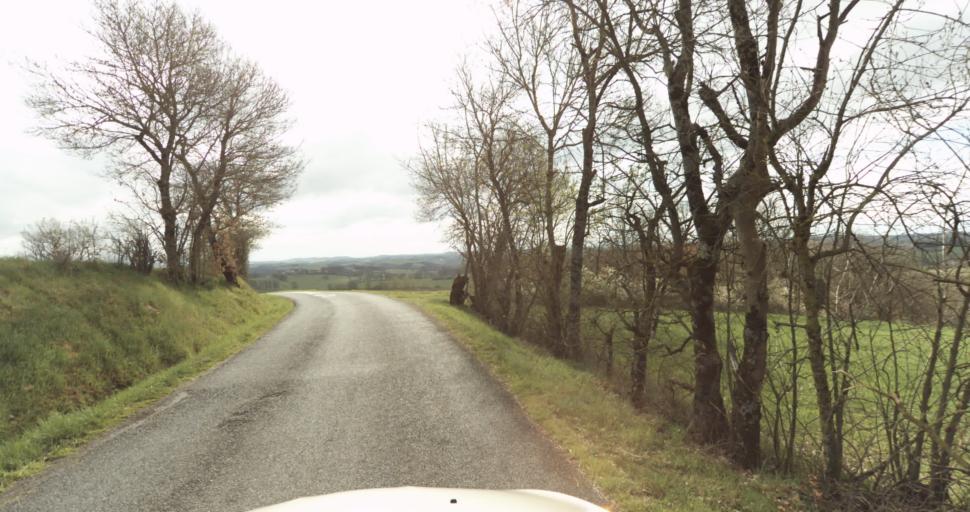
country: FR
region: Midi-Pyrenees
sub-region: Departement du Tarn
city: Frejairolles
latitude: 43.8659
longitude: 2.2102
